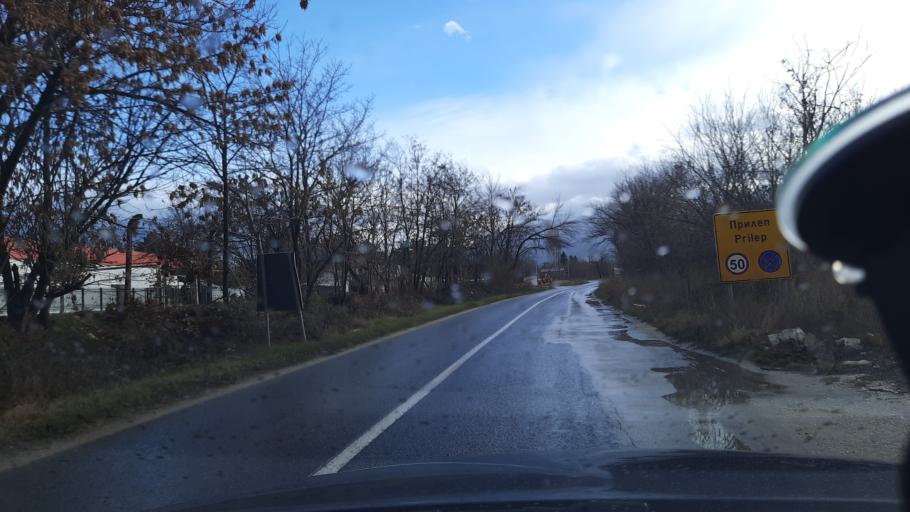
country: MK
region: Prilep
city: Markov Grad
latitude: 41.3434
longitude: 21.5185
